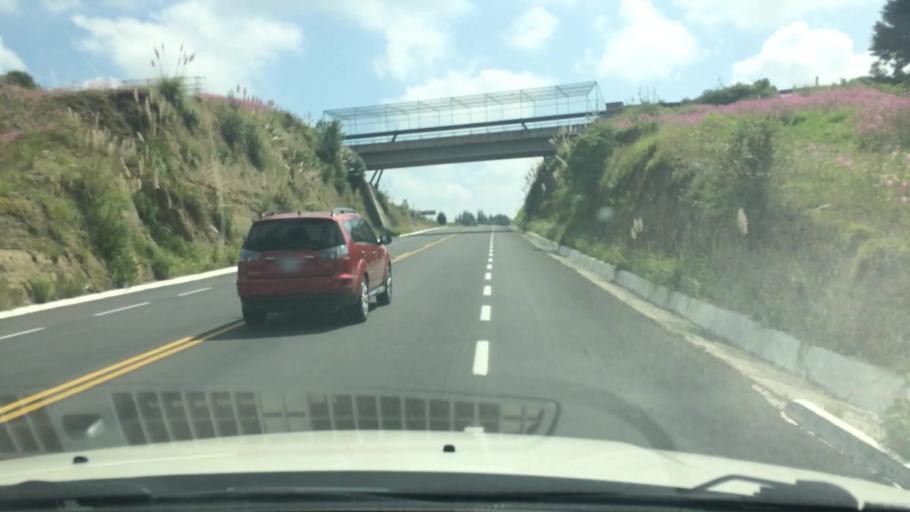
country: MX
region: Mexico
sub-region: Villa Victoria
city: Colonia Doctor Gustavo Baz
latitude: 19.3771
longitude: -99.8846
